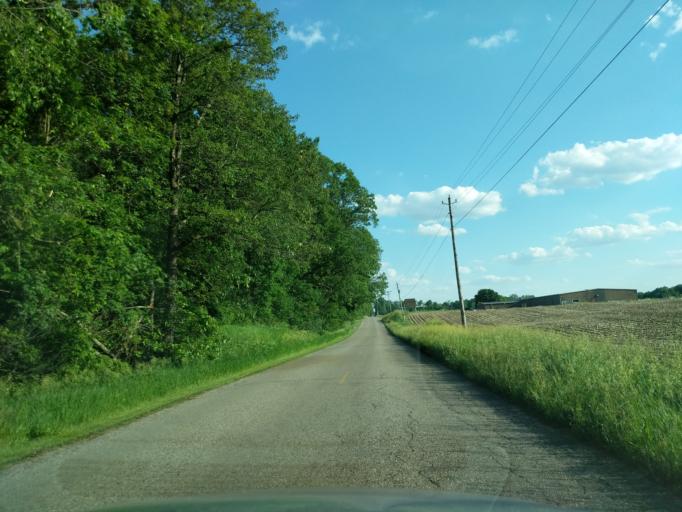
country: US
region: Indiana
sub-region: Kosciusko County
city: North Webster
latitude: 41.3052
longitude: -85.6334
